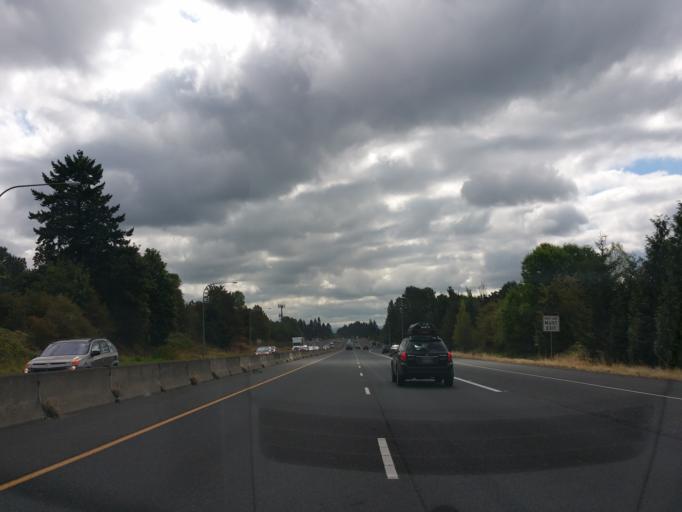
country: US
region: Washington
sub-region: Clark County
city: Mill Plain
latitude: 45.5946
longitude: -122.5147
